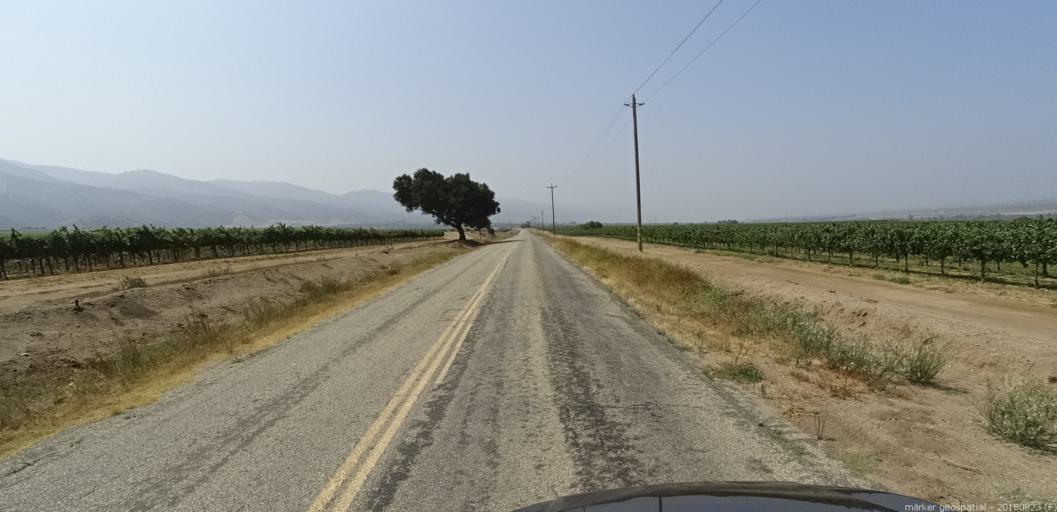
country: US
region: California
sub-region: Monterey County
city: Gonzales
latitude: 36.4338
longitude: -121.4201
